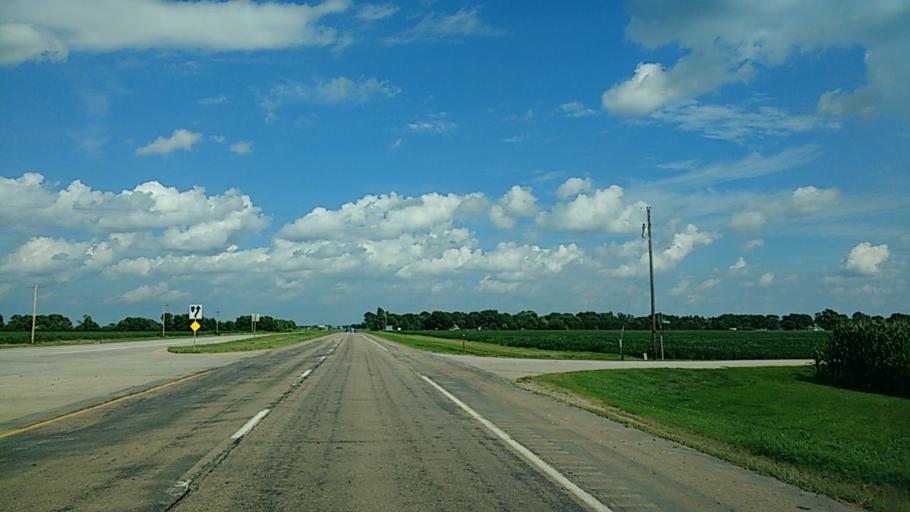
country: US
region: South Dakota
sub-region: Union County
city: Dakota Dunes
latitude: 42.4482
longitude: -96.5373
